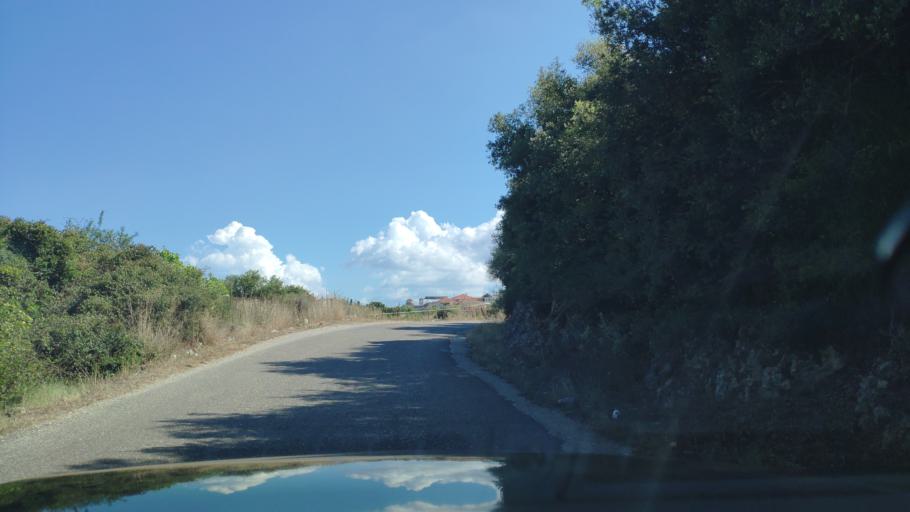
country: GR
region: West Greece
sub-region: Nomos Aitolias kai Akarnanias
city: Katouna
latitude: 38.7937
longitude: 21.1151
